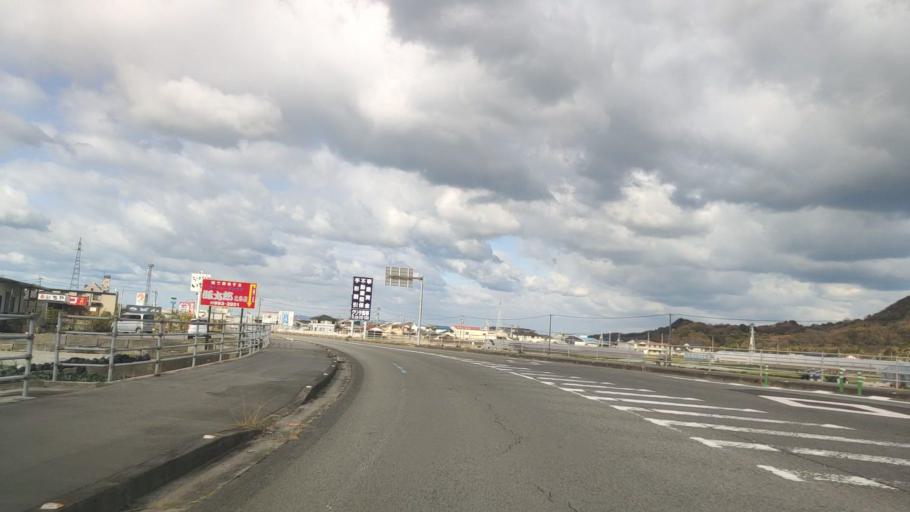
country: JP
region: Ehime
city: Hojo
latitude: 33.9804
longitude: 132.7853
